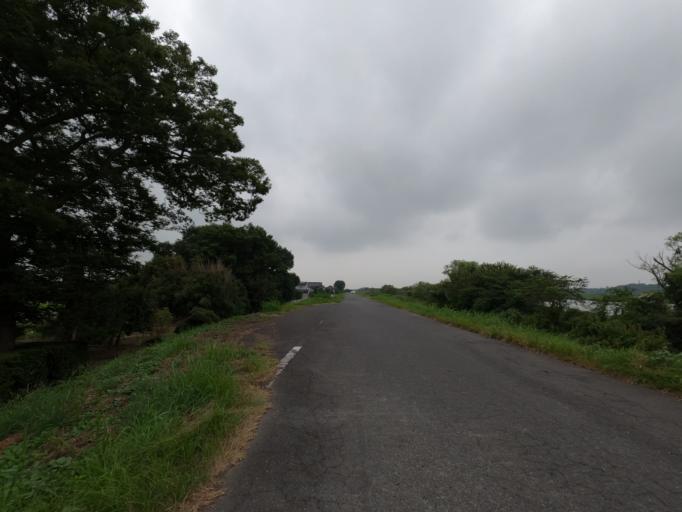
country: JP
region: Ibaraki
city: Moriya
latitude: 35.9394
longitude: 140.0341
